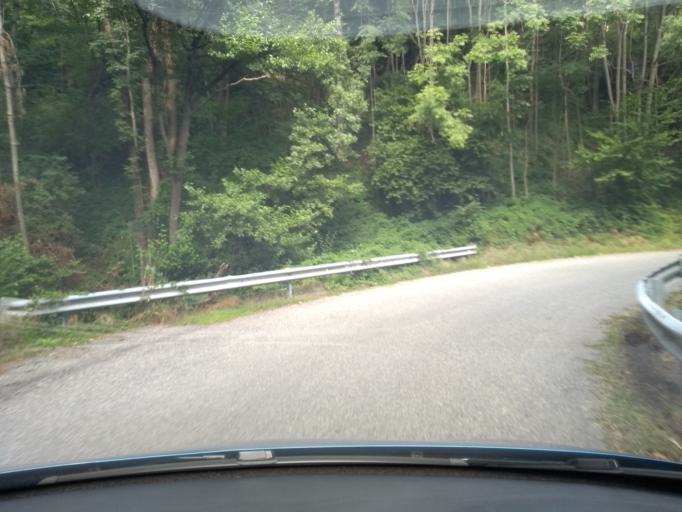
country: IT
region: Piedmont
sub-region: Provincia di Torino
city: Corio
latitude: 45.3059
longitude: 7.5087
